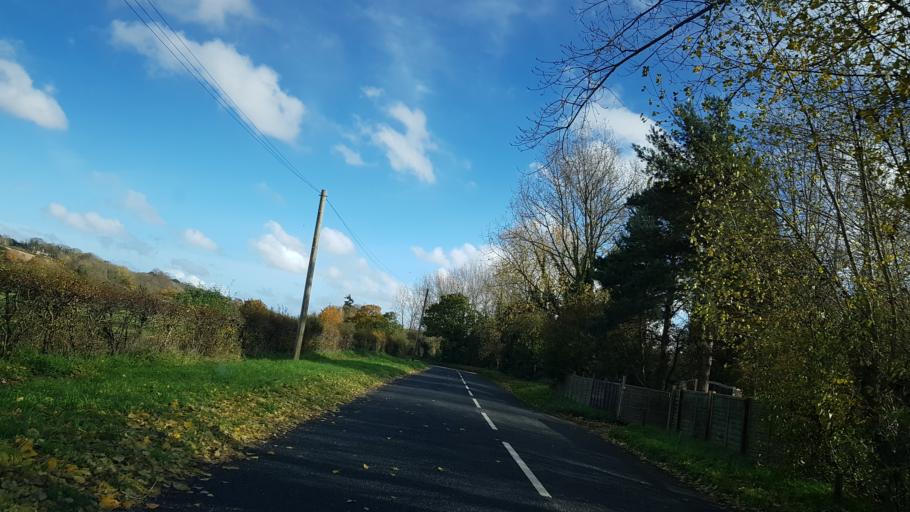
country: GB
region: England
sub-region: Surrey
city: Seale
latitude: 51.2228
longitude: -0.7263
